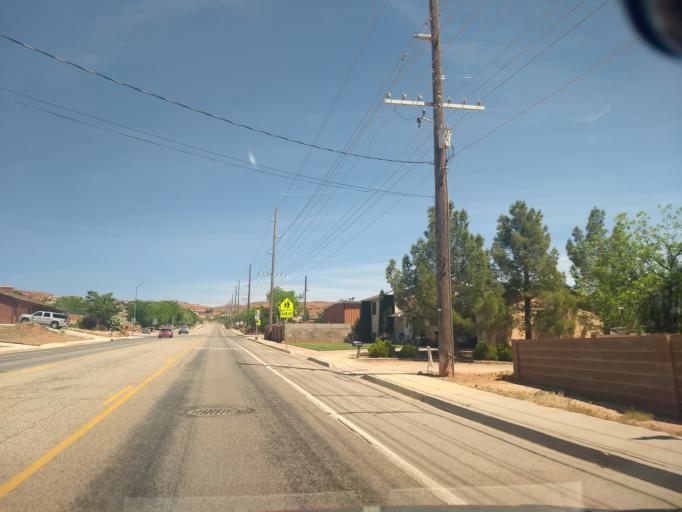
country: US
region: Utah
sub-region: Washington County
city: Santa Clara
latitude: 37.1430
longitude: -113.6296
